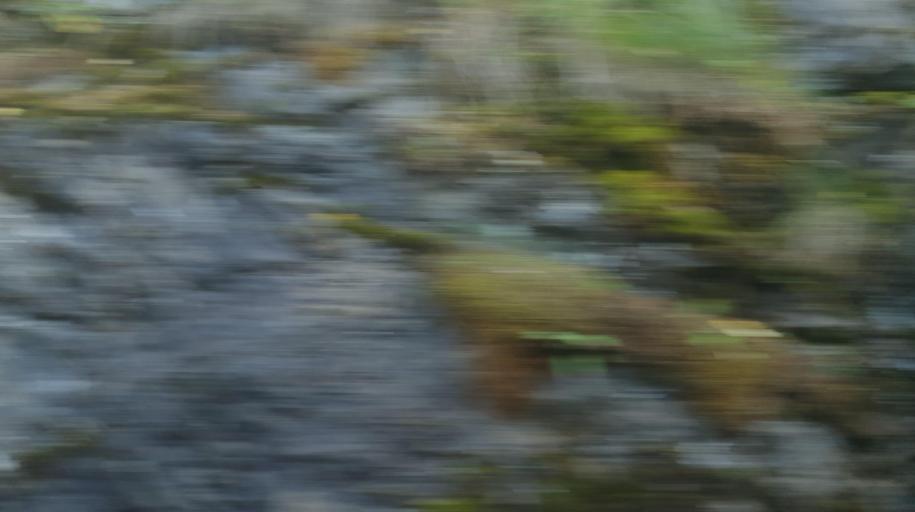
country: NO
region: Nord-Trondelag
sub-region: Frosta
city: Frosta
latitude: 63.5343
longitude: 10.8232
